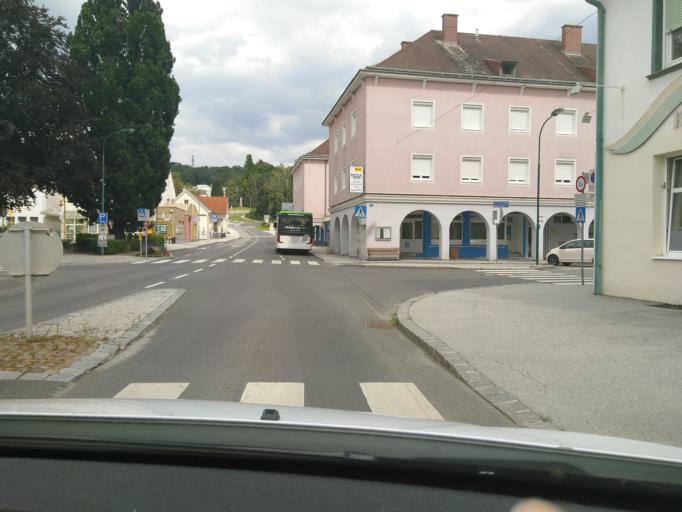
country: AT
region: Burgenland
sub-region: Politischer Bezirk Oberwart
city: Oberschutzen
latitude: 47.3507
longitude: 16.2071
